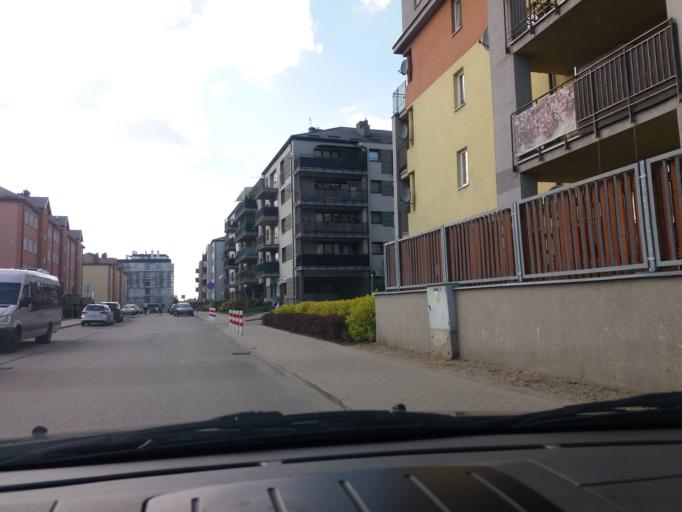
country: PL
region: Masovian Voivodeship
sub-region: Powiat mlawski
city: Mlawa
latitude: 53.1225
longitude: 20.3666
